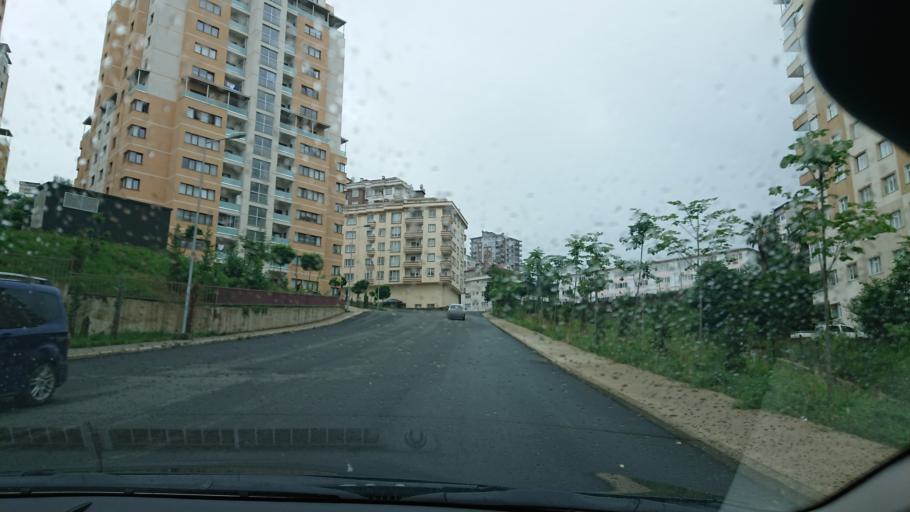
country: TR
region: Rize
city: Rize
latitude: 41.0167
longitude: 40.5145
